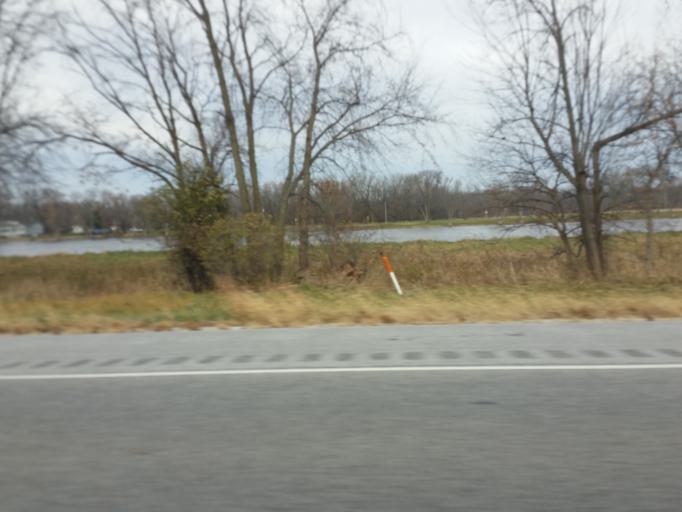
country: US
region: Illinois
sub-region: Rock Island County
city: Coal Valley
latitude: 41.4544
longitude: -90.4692
